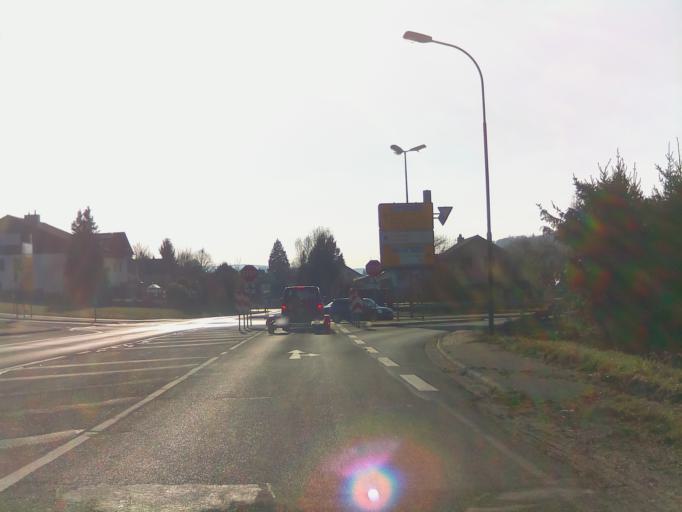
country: DE
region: Hesse
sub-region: Regierungsbezirk Darmstadt
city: Schluchtern
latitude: 50.3532
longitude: 9.5391
